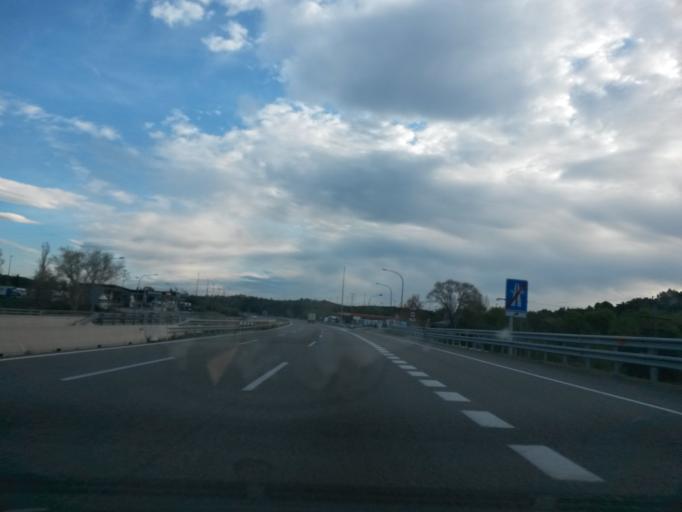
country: ES
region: Catalonia
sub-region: Provincia de Girona
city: Pontos
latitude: 42.1715
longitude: 2.9295
